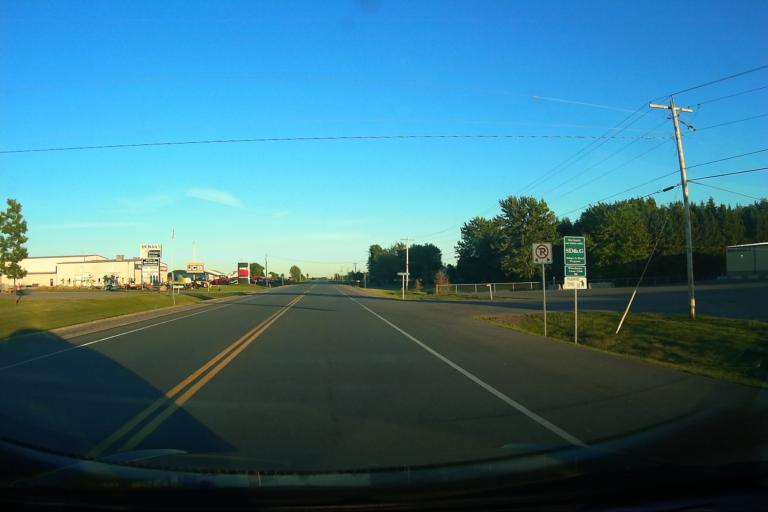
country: CA
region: Ontario
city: Casselman
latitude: 45.0821
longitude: -75.3722
